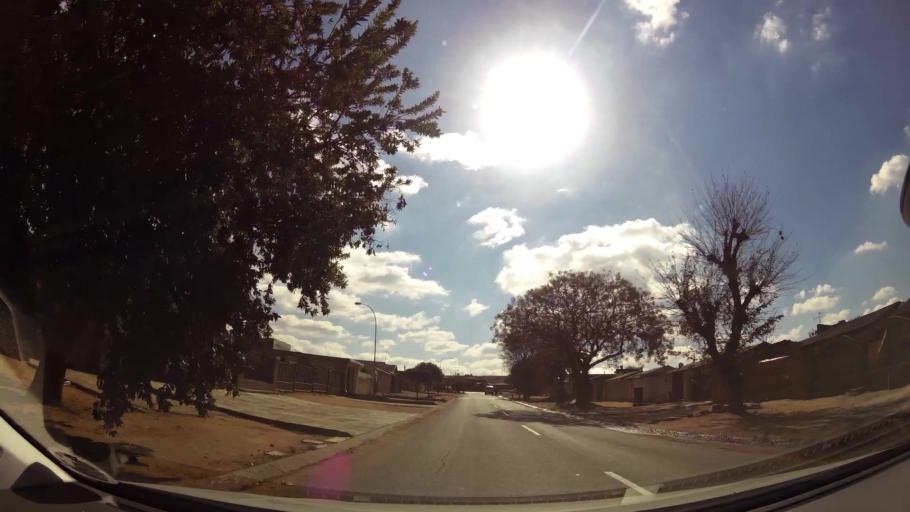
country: ZA
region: Gauteng
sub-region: City of Johannesburg Metropolitan Municipality
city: Roodepoort
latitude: -26.2077
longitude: 27.8806
